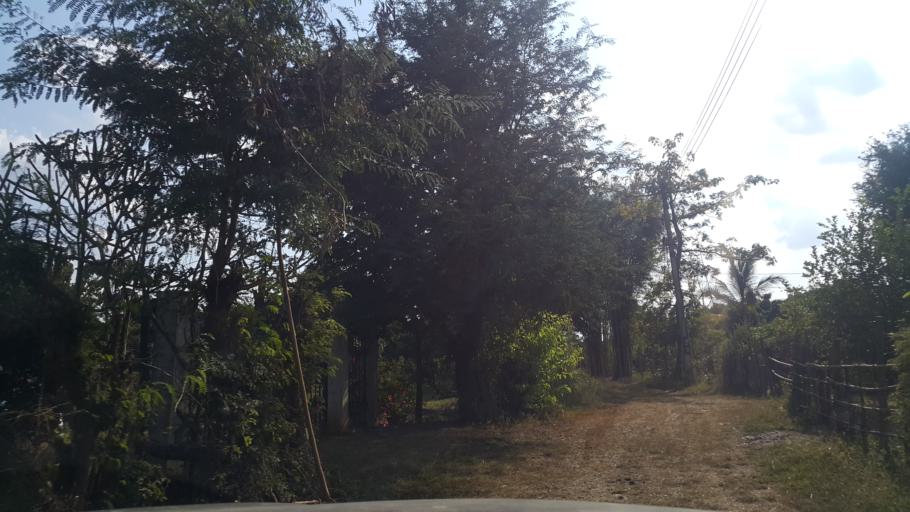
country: TH
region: Lamphun
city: Ban Thi
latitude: 18.5659
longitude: 99.1233
